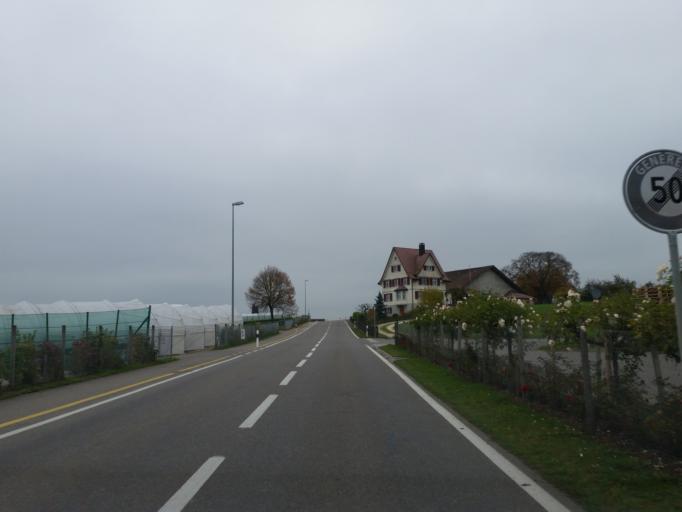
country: CH
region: Thurgau
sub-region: Arbon District
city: Uttwil
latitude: 47.5859
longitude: 9.3158
